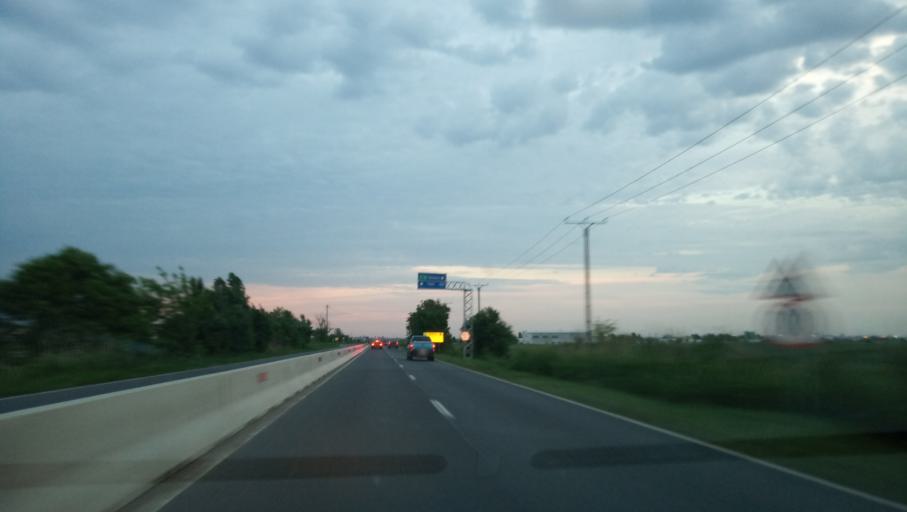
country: RO
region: Timis
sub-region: Comuna Sag
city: Sag
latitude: 45.6803
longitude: 21.1693
